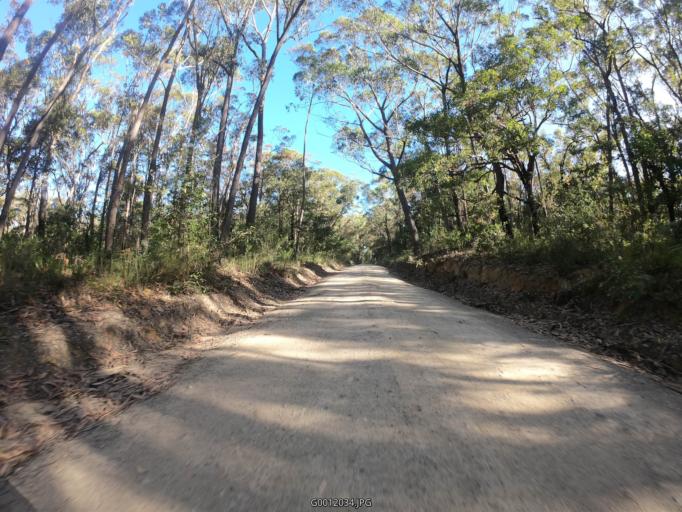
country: AU
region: New South Wales
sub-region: Lake Macquarie Shire
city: Cooranbong
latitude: -33.0674
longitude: 151.3351
